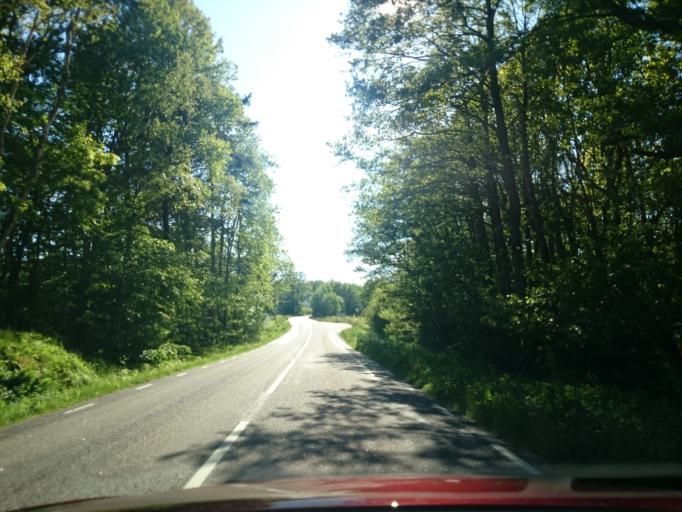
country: SE
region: Vaestra Goetaland
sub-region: Lysekils Kommun
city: Lysekil
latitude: 58.2498
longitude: 11.4839
